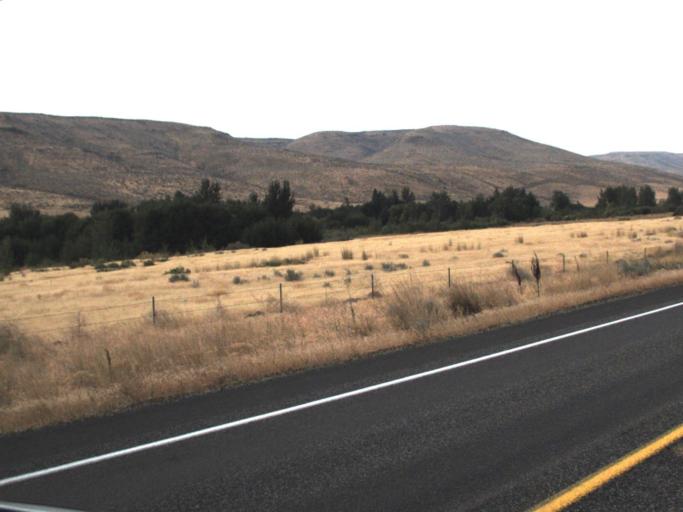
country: US
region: Washington
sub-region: Yakima County
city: Toppenish
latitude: 46.1847
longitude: -120.4958
